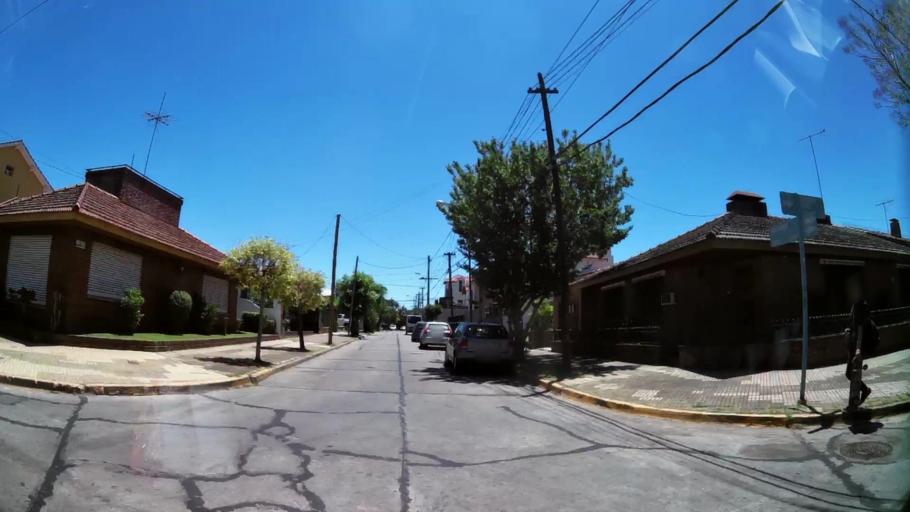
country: AR
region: Buenos Aires
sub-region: Partido de Tigre
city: Tigre
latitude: -34.4452
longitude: -58.5469
